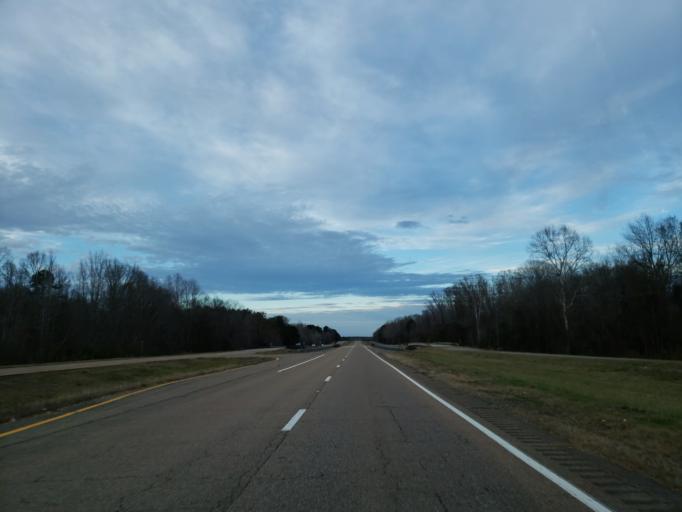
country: US
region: Mississippi
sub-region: Lauderdale County
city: Meridian Station
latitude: 32.5281
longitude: -88.5127
